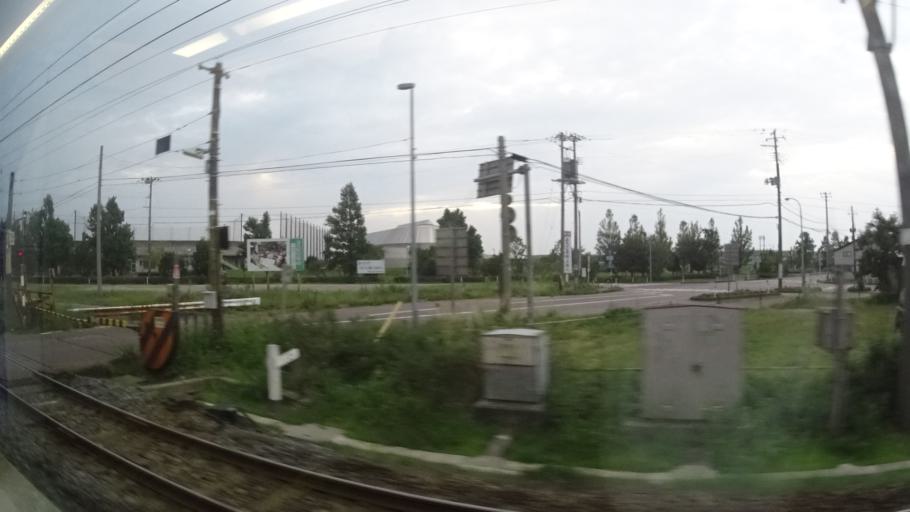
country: JP
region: Niigata
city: Murakami
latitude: 38.1811
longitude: 139.4597
